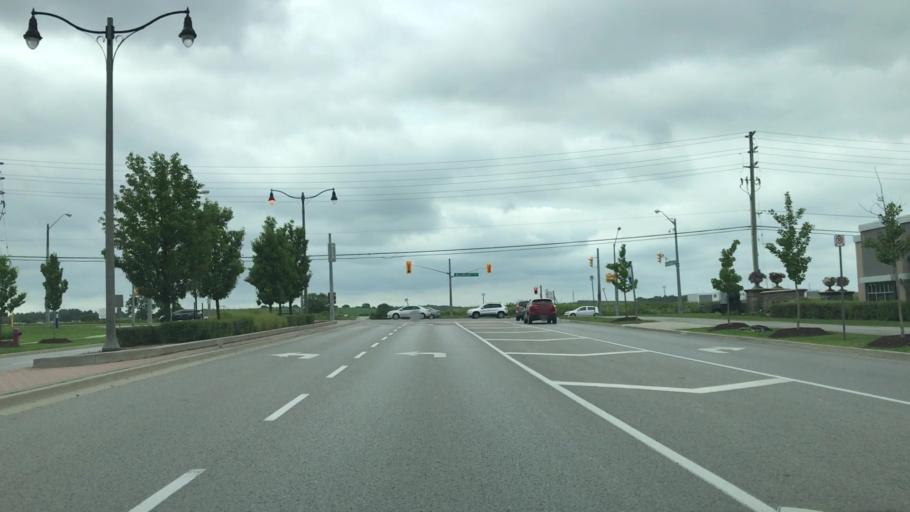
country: CA
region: Ontario
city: Newmarket
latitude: 44.0128
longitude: -79.4149
